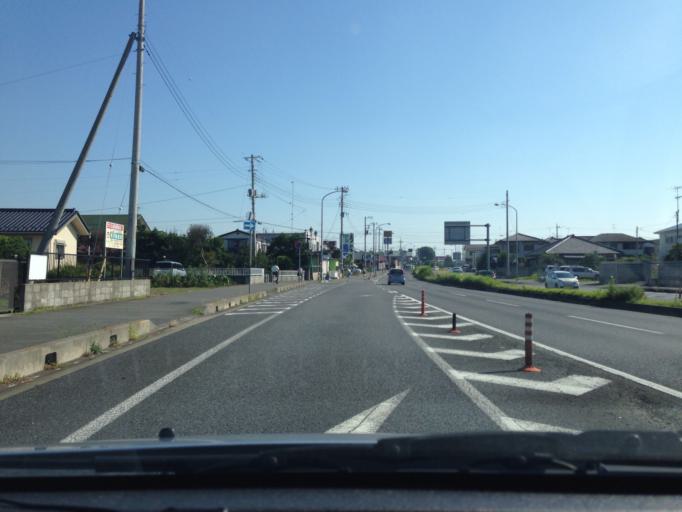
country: JP
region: Ibaraki
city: Naka
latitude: 36.0371
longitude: 140.1738
